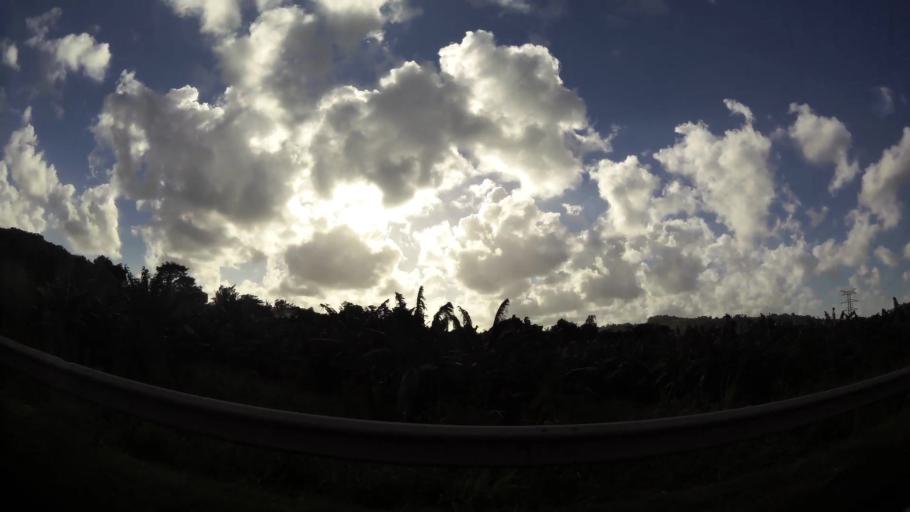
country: MQ
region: Martinique
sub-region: Martinique
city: Ducos
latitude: 14.6015
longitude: -60.9651
